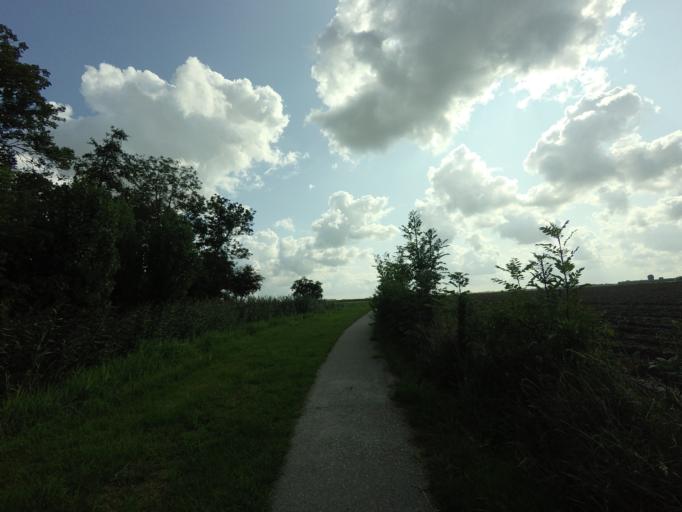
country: NL
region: Friesland
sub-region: Gemeente Het Bildt
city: Sint Jacobiparochie
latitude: 53.2695
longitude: 5.6056
